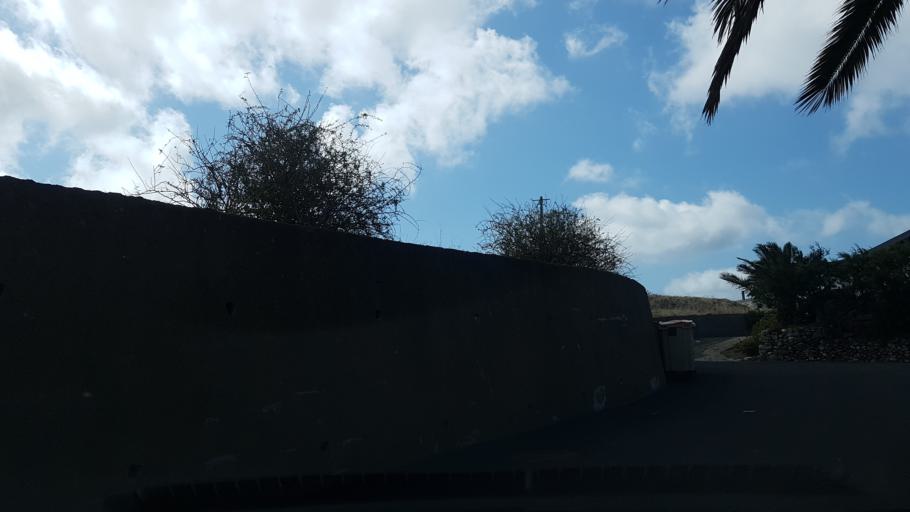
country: PT
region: Madeira
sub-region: Porto Santo
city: Vila de Porto Santo
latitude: 33.0717
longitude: -16.3259
